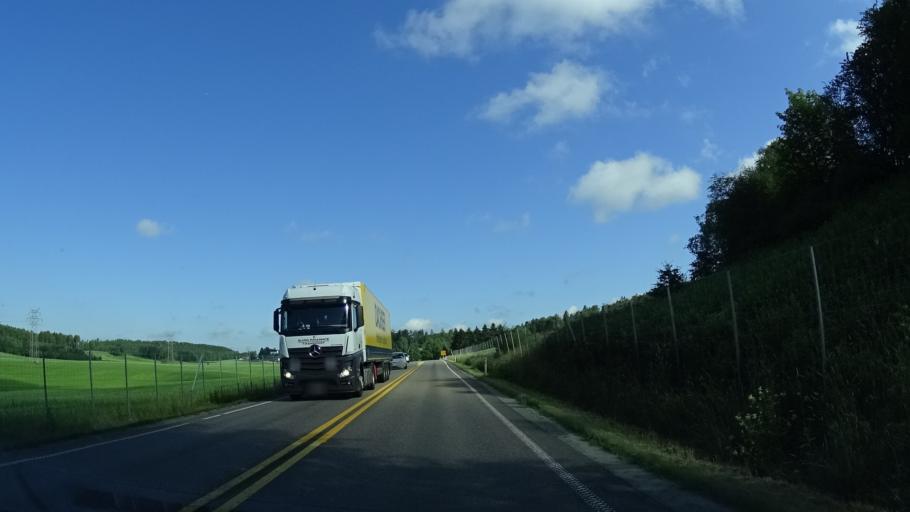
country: NO
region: Ostfold
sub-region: Hobol
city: Elvestad
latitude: 59.6519
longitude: 10.9211
